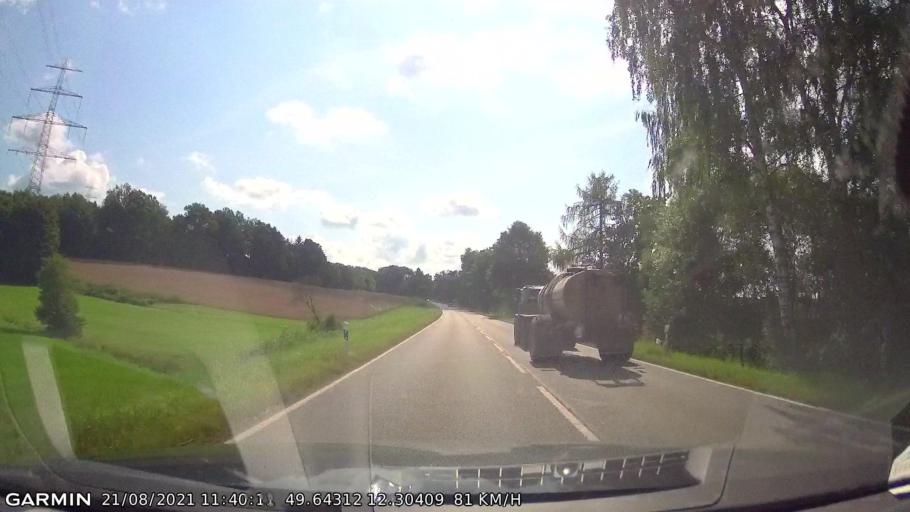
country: DE
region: Bavaria
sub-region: Upper Palatinate
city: Waldthurn
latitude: 49.6430
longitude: 12.3042
